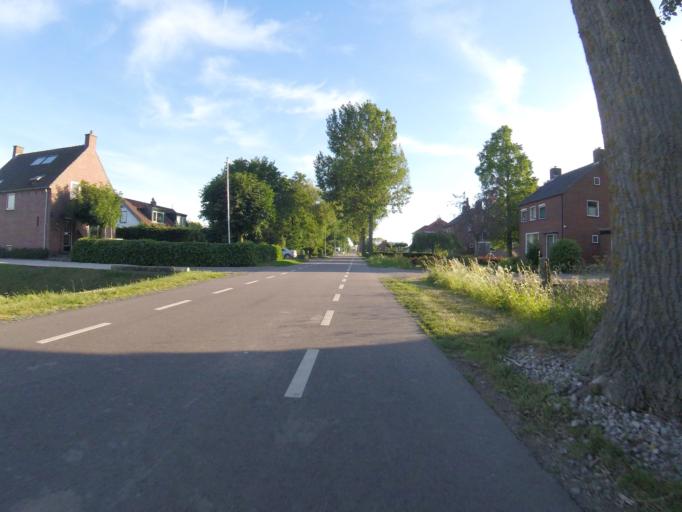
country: NL
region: North Holland
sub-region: Gemeente Haarlemmermeer
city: Hoofddorp
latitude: 52.2992
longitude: 4.7234
